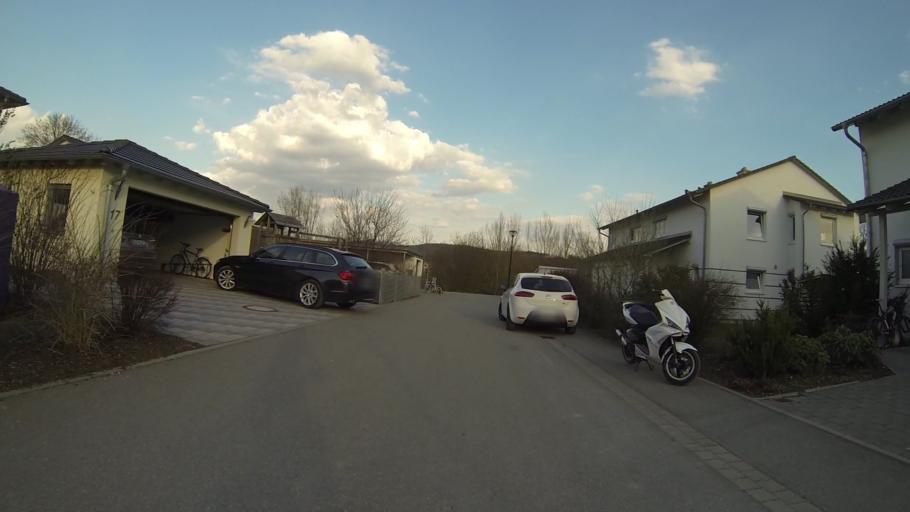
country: DE
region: Baden-Wuerttemberg
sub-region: Regierungsbezirk Stuttgart
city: Heidenheim an der Brenz
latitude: 48.6952
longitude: 10.1614
